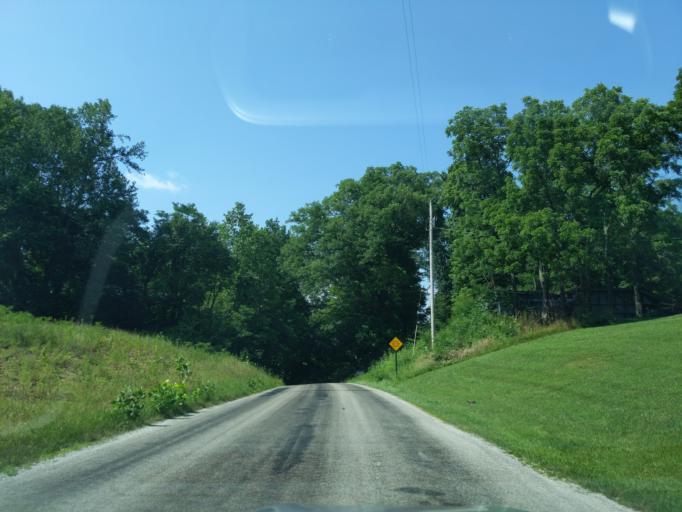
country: US
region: Indiana
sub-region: Ripley County
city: Osgood
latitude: 39.1098
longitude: -85.3438
